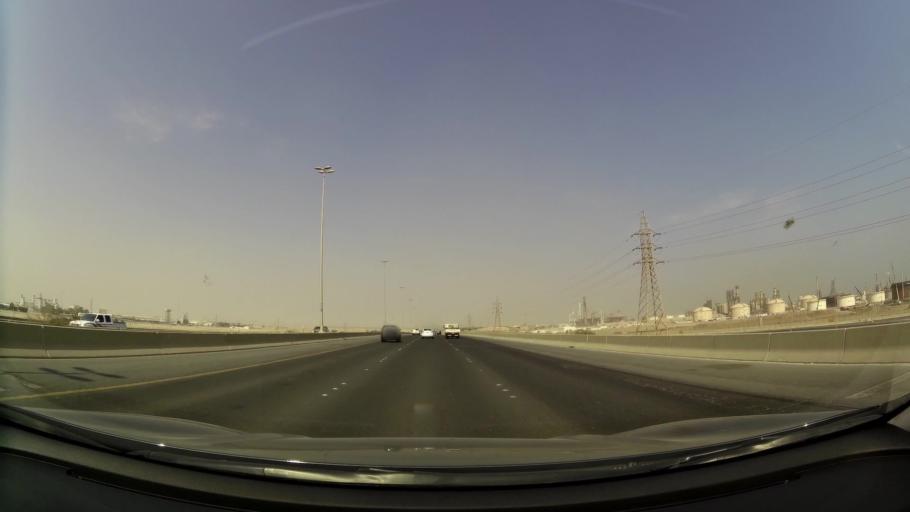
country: KW
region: Al Ahmadi
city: Al Fahahil
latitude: 29.0117
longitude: 48.1324
